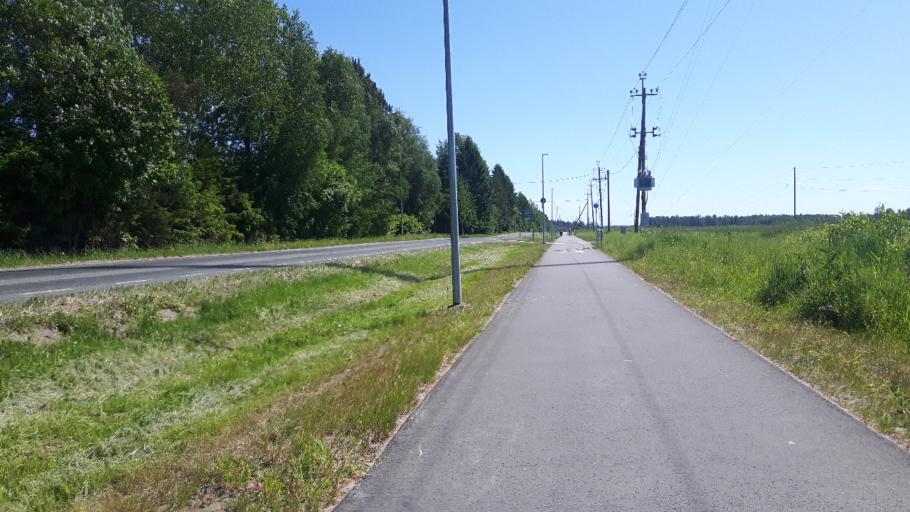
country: EE
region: Harju
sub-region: Saku vald
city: Saku
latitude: 59.2160
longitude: 24.6772
